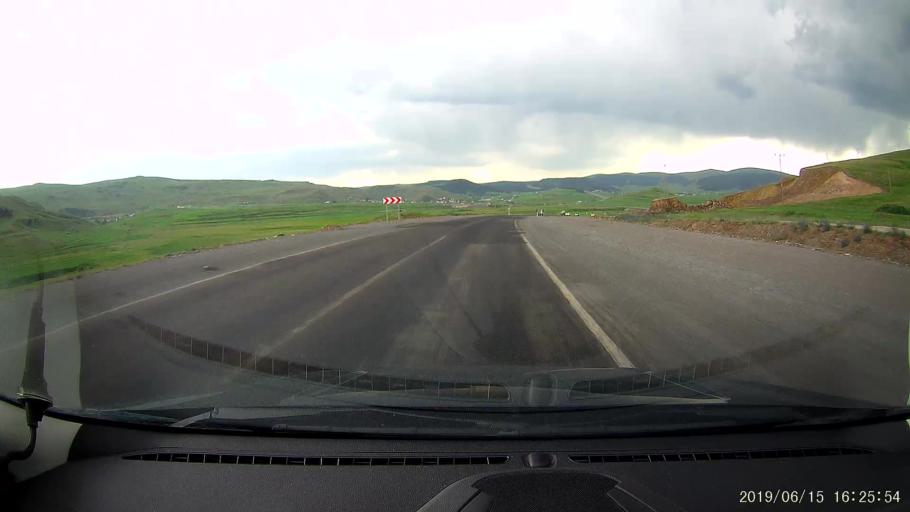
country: TR
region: Ardahan
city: Hanak
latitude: 41.1479
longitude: 42.8658
